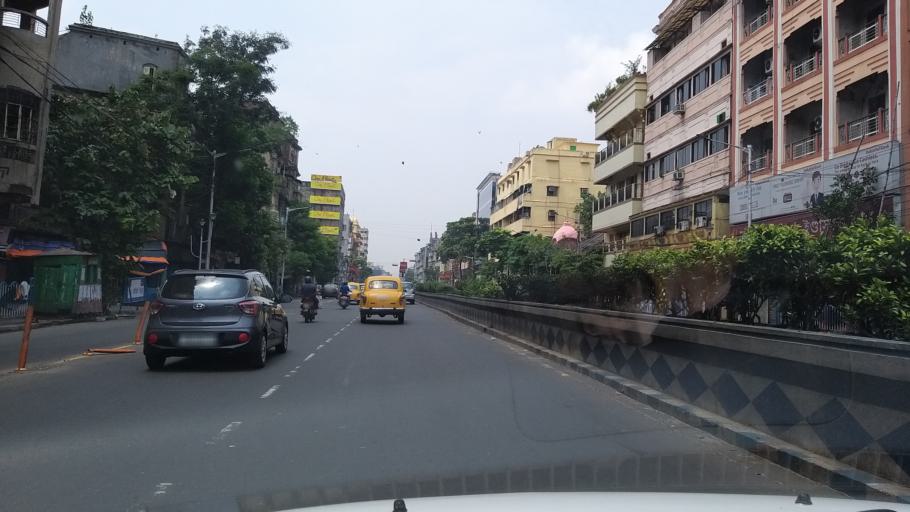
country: IN
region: West Bengal
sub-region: Kolkata
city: Bara Bazar
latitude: 22.5854
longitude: 88.3625
